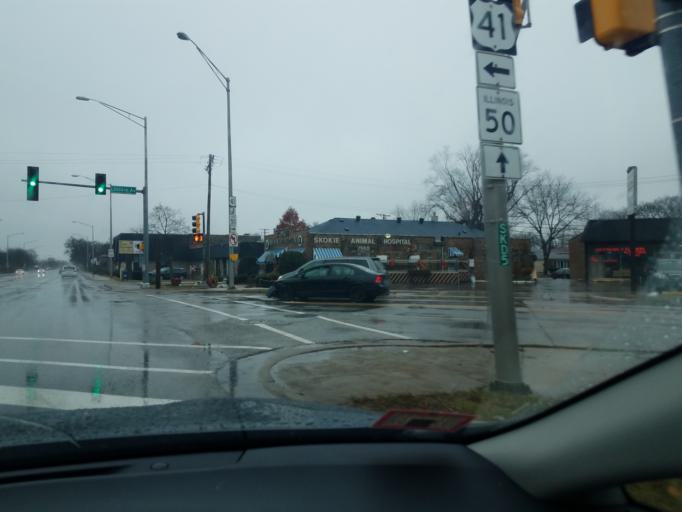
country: US
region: Illinois
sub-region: Cook County
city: Skokie
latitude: 42.0186
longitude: -87.7478
